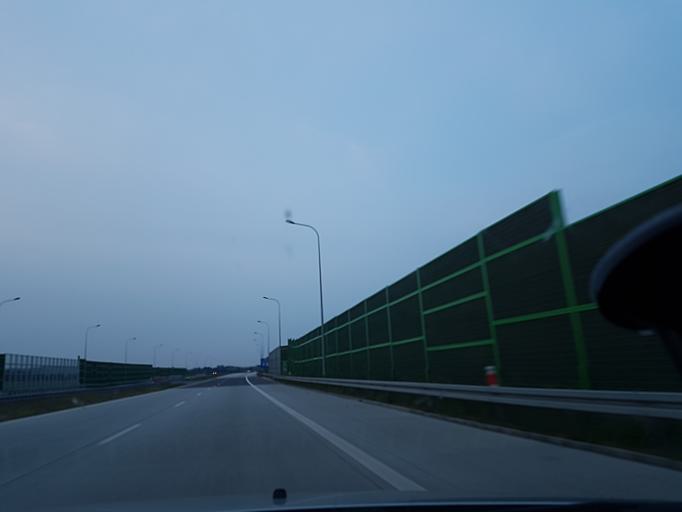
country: PL
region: Lodz Voivodeship
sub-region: Powiat zgierski
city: Strykow
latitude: 51.8475
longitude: 19.6598
